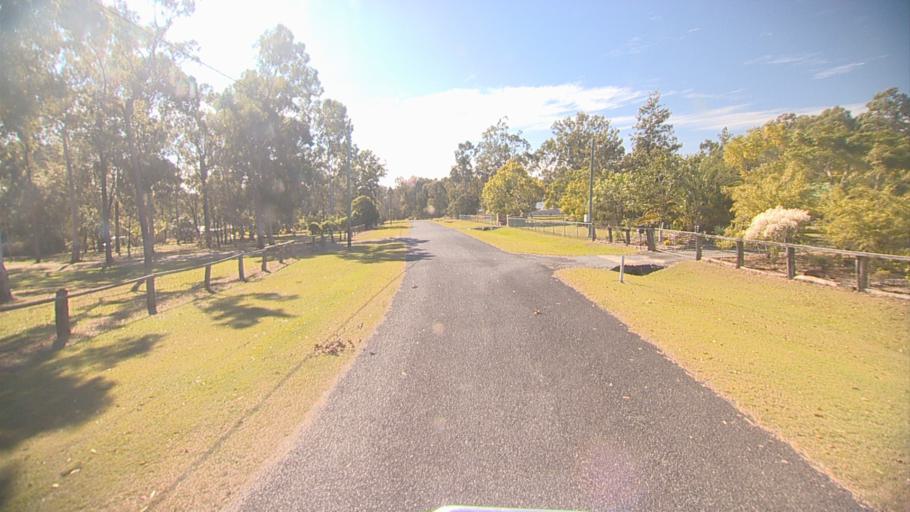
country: AU
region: Queensland
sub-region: Ipswich
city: Springfield Lakes
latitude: -27.7145
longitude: 152.9541
